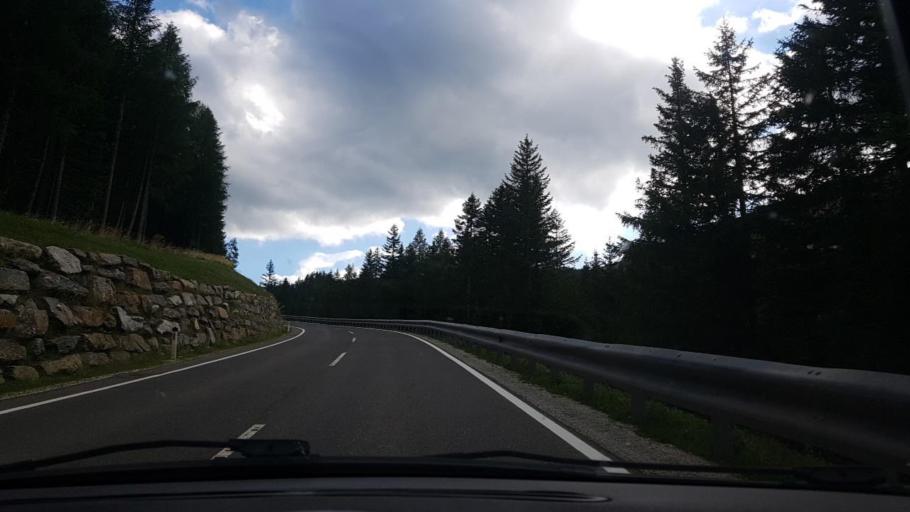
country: AT
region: Salzburg
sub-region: Politischer Bezirk Tamsweg
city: Sankt Michael im Lungau
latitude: 47.0635
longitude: 13.6140
